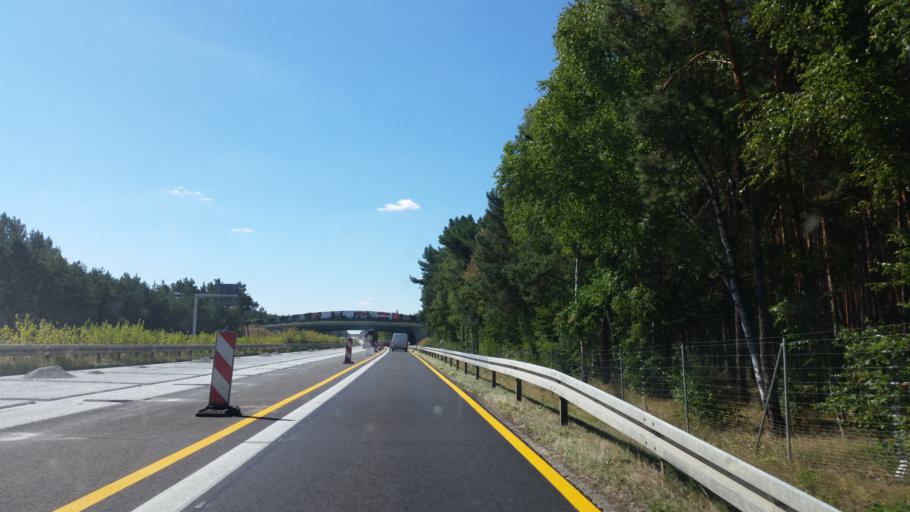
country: DE
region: Brandenburg
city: Teupitz
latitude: 52.1118
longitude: 13.6462
